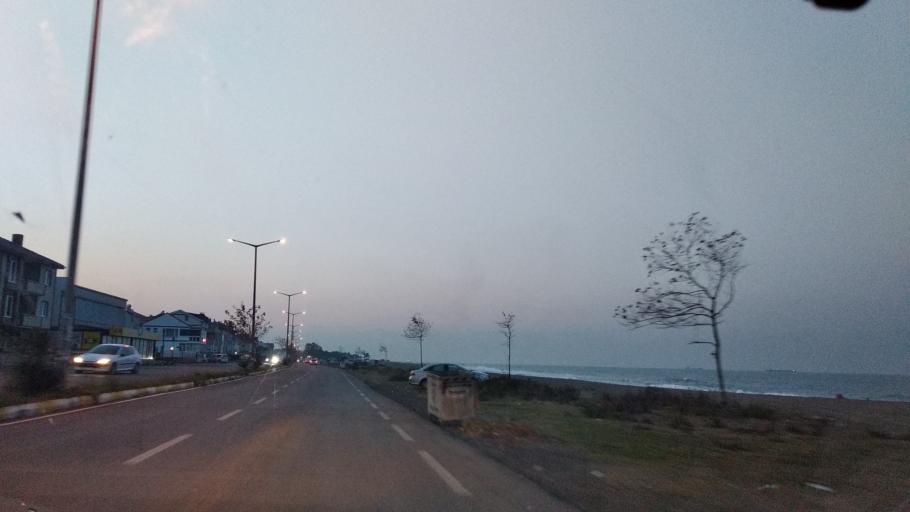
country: TR
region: Sakarya
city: Karasu
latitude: 41.0915
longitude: 30.7413
